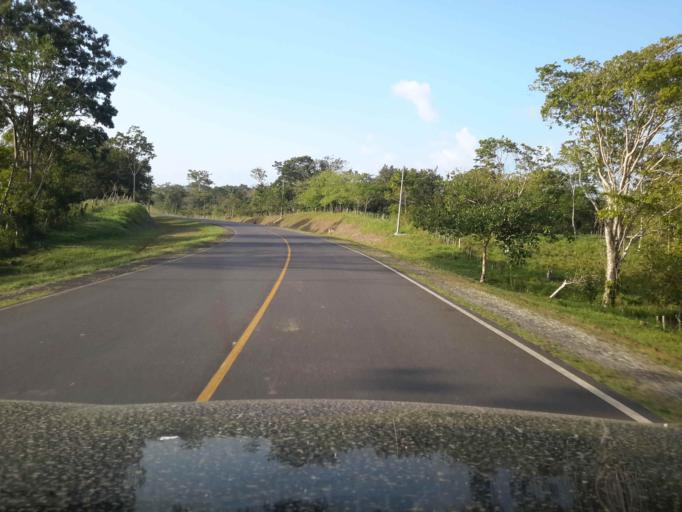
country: NI
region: Rio San Juan
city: San Carlos
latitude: 11.2168
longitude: -84.6876
